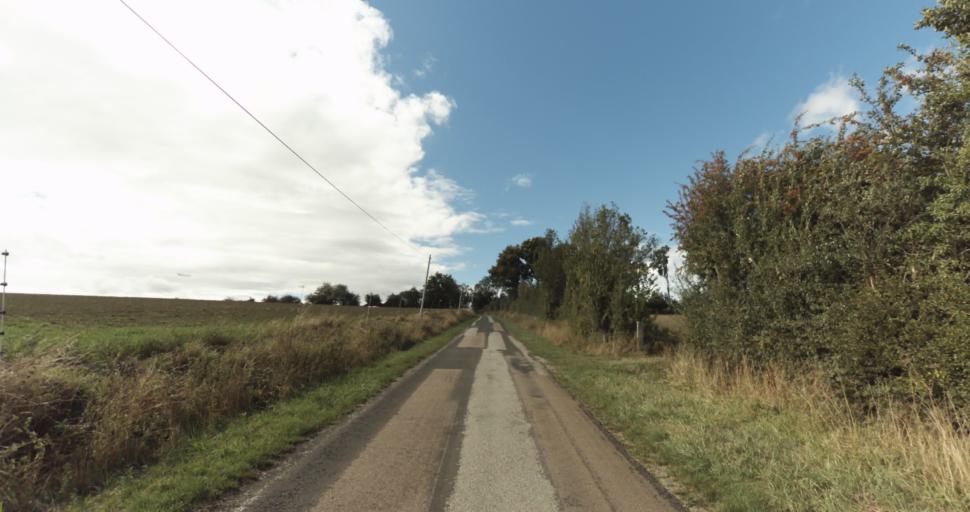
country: FR
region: Lower Normandy
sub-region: Departement de l'Orne
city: Gace
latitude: 48.7743
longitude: 0.3380
